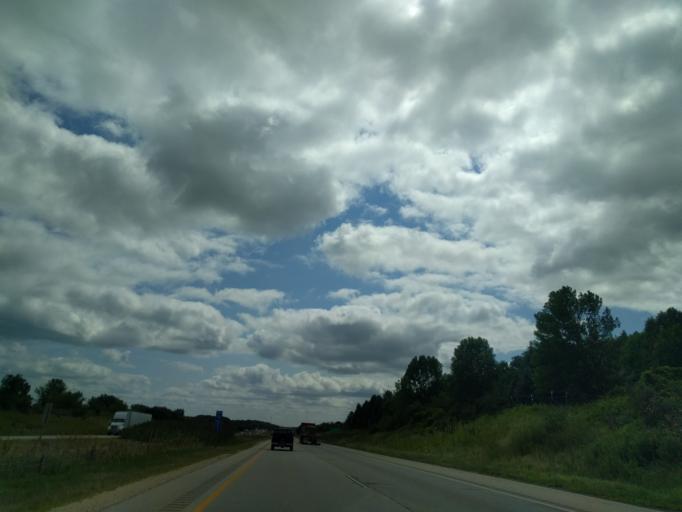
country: US
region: Wisconsin
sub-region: Ozaukee County
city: Grafton
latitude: 43.3025
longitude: -87.9207
